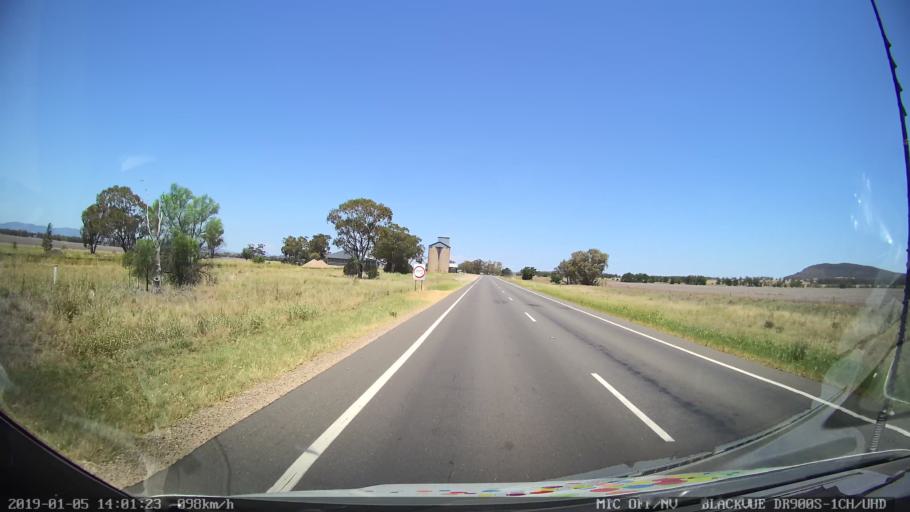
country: AU
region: New South Wales
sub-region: Gunnedah
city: Gunnedah
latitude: -31.1692
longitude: 150.3244
